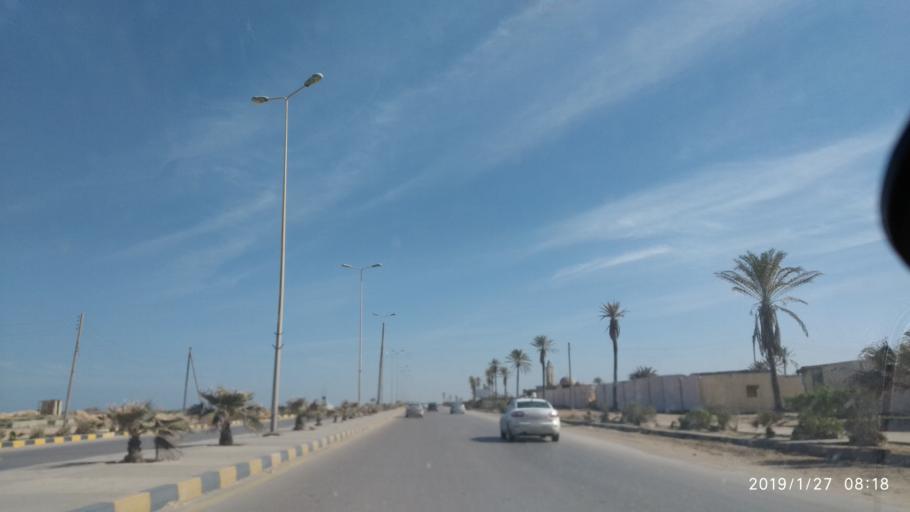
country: LY
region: Tripoli
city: Tagiura
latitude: 32.8951
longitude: 13.3331
